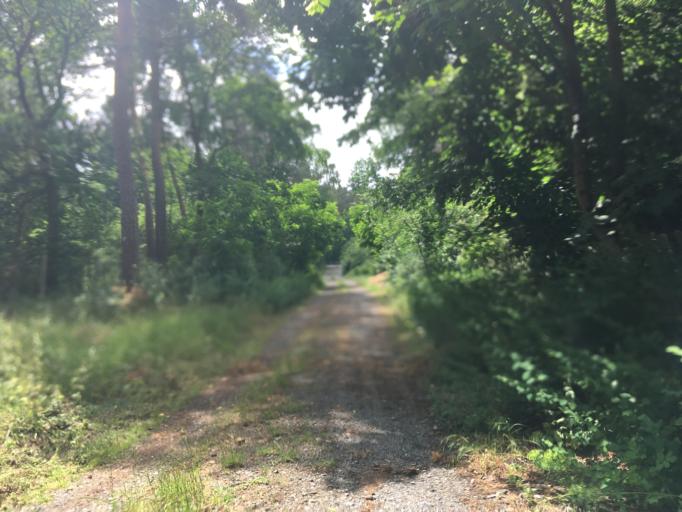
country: DE
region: Berlin
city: Muggelheim
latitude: 52.4081
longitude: 13.6725
